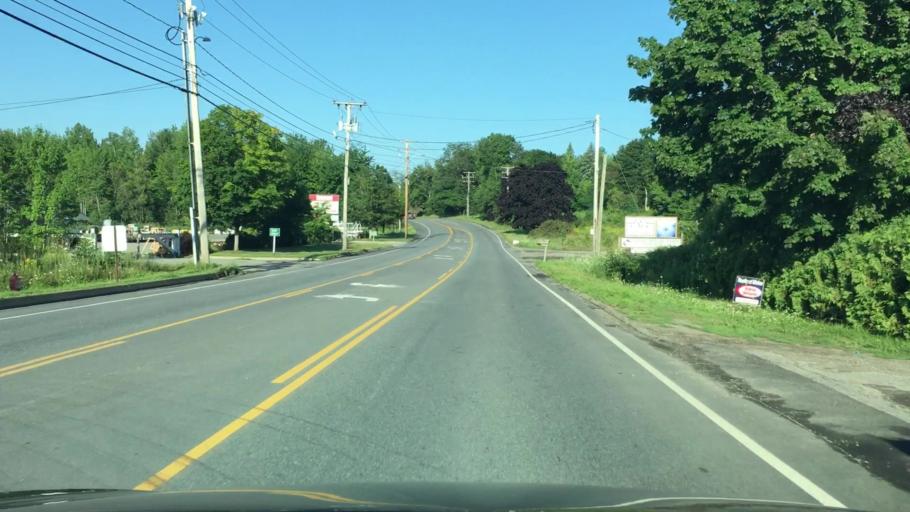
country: US
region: Maine
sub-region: Waldo County
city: Belfast
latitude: 44.4231
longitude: -69.0266
